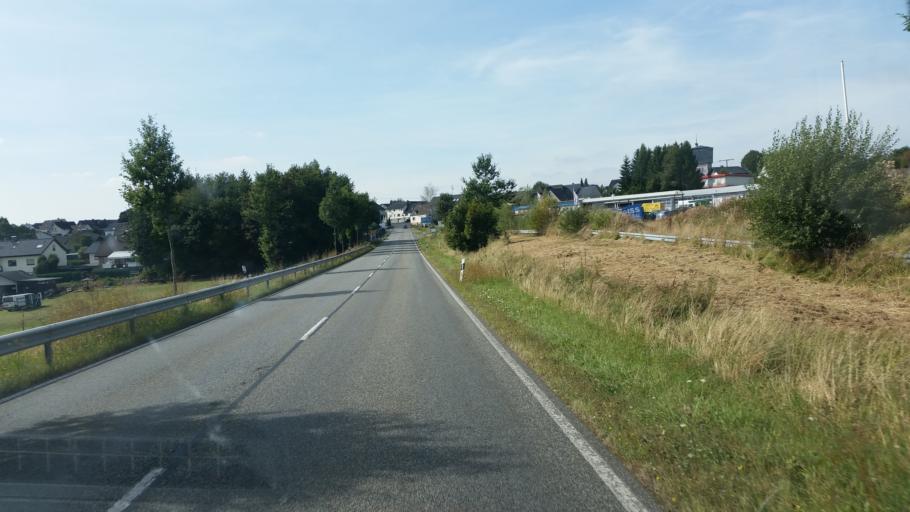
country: DE
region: Rheinland-Pfalz
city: Hohn
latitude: 50.6180
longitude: 7.9931
